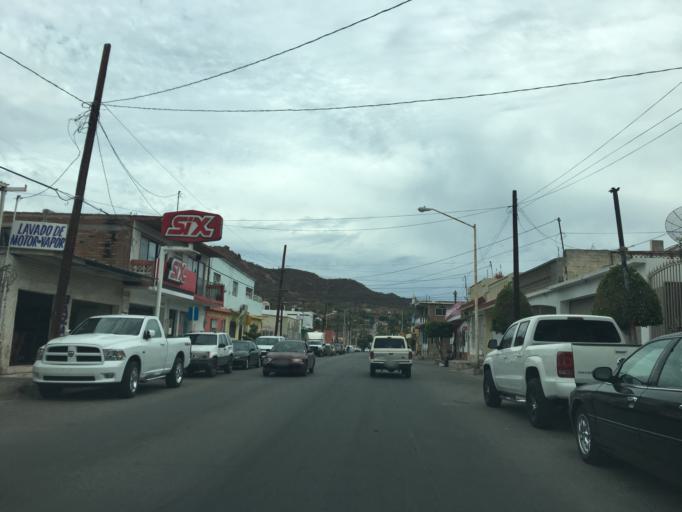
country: MX
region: Sonora
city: Heroica Guaymas
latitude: 27.9205
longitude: -110.8990
